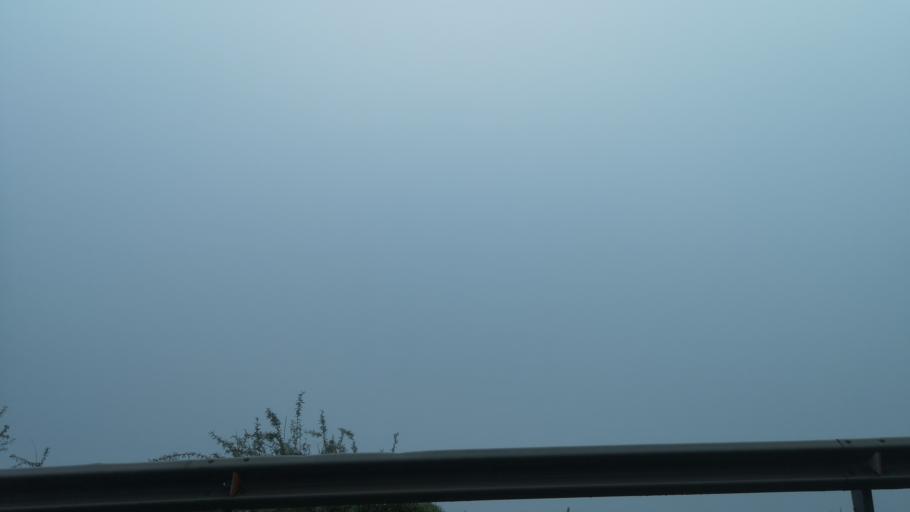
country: ES
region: Canary Islands
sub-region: Provincia de Santa Cruz de Tenerife
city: Alajero
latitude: 28.0990
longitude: -17.1872
